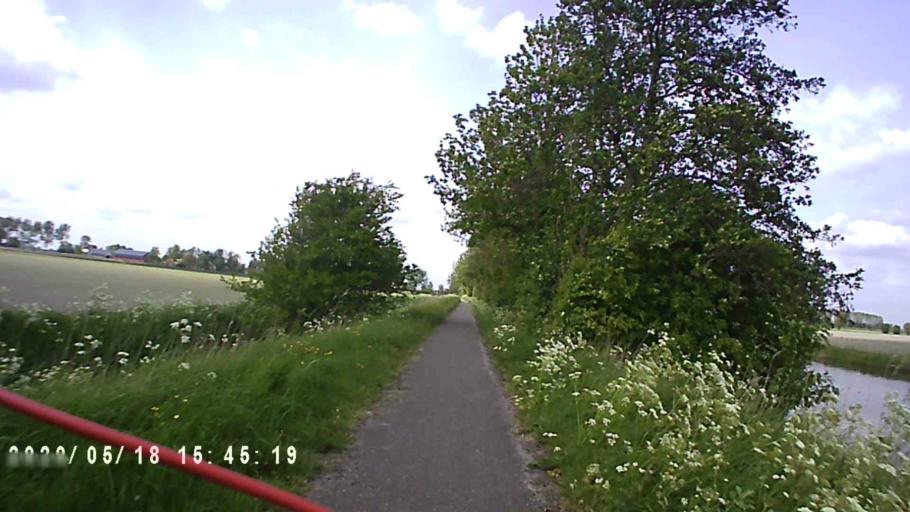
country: NL
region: Groningen
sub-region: Gemeente Winsum
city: Winsum
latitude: 53.3143
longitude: 6.4706
